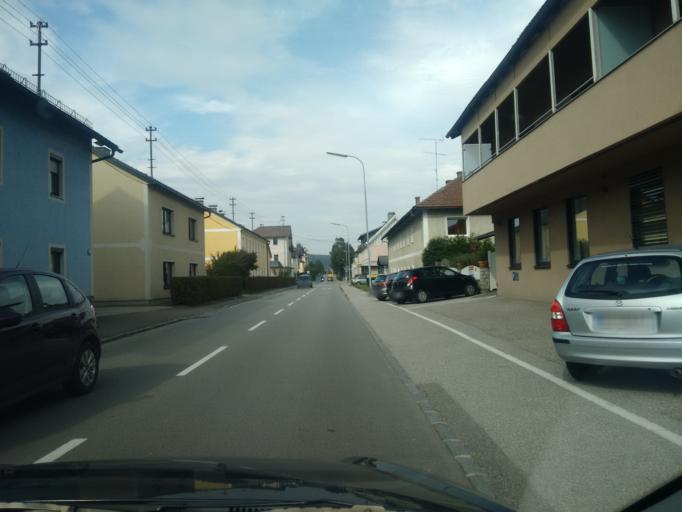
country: AT
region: Upper Austria
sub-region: Politischer Bezirk Vocklabruck
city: Attnang-Puchheim
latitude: 48.0022
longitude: 13.7159
